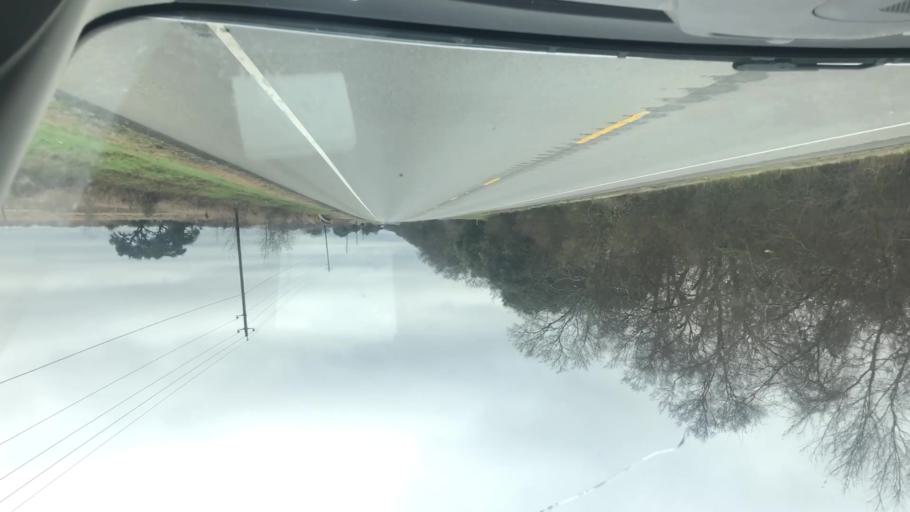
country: US
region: Texas
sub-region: Matagorda County
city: Bay City
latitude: 29.0759
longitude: -95.9726
